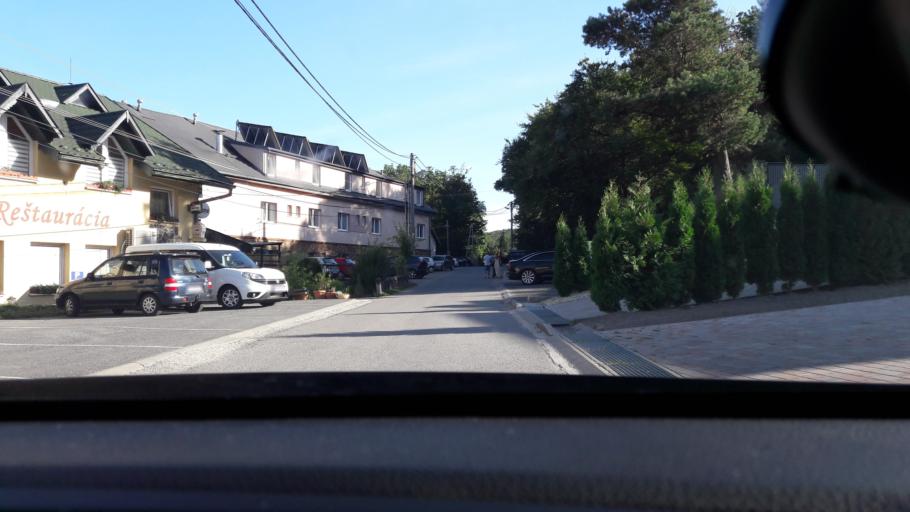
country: SK
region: Kosicky
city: Vinne
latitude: 48.8191
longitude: 21.9840
